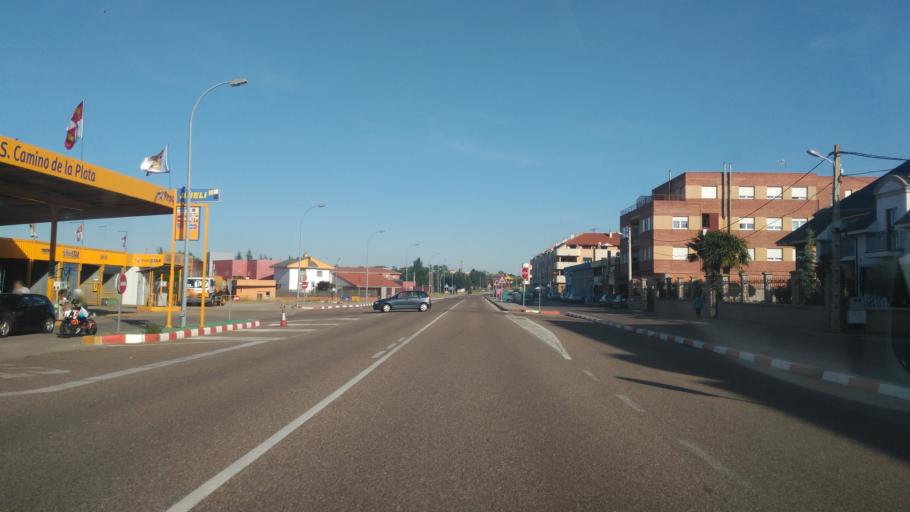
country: ES
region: Castille and Leon
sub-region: Provincia de Zamora
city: Morales del Vino
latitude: 41.4448
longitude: -5.7341
